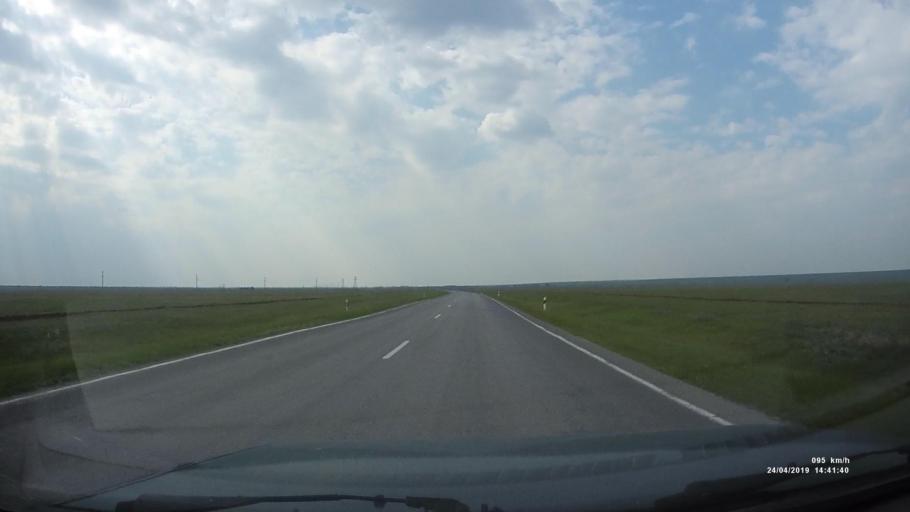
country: RU
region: Rostov
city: Remontnoye
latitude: 46.4471
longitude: 43.8761
